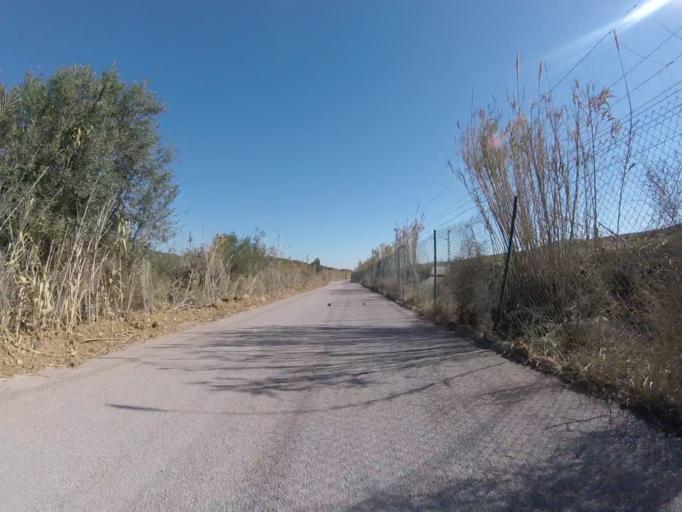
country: ES
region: Valencia
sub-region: Provincia de Castello
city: Santa Magdalena de Pulpis
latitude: 40.3393
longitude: 0.2595
